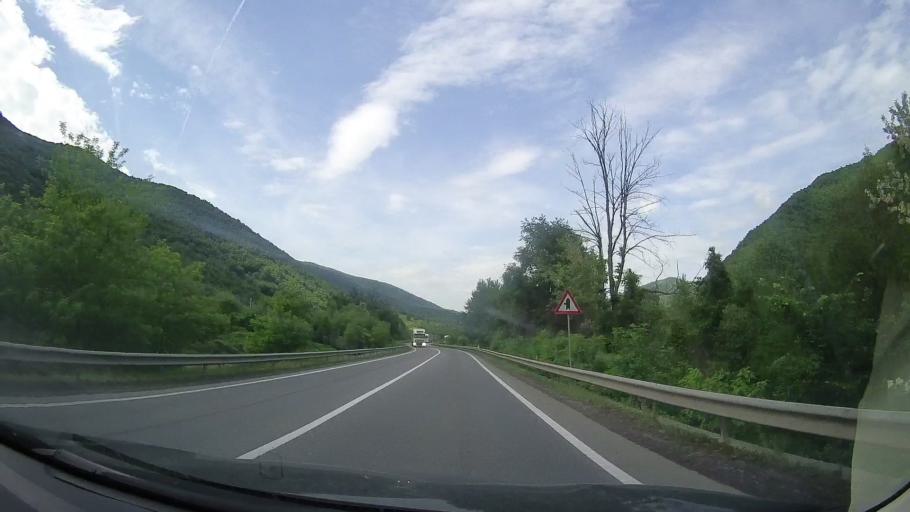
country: RO
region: Caras-Severin
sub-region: Oras Baile Herculane
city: Baile Herculane
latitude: 44.8434
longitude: 22.3829
